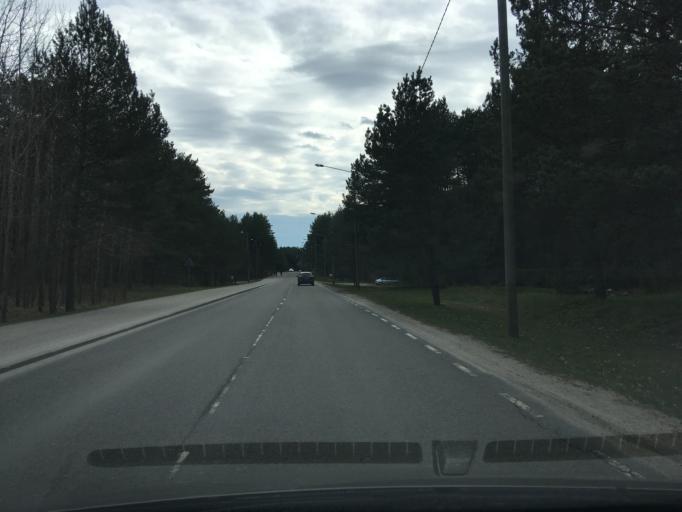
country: EE
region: Harju
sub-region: Tallinna linn
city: Kose
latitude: 59.4718
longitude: 24.9104
